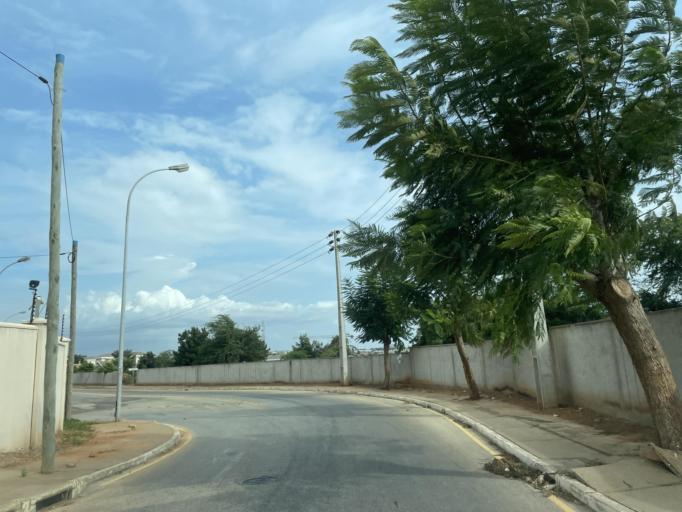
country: AO
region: Luanda
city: Luanda
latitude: -8.9302
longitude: 13.1794
